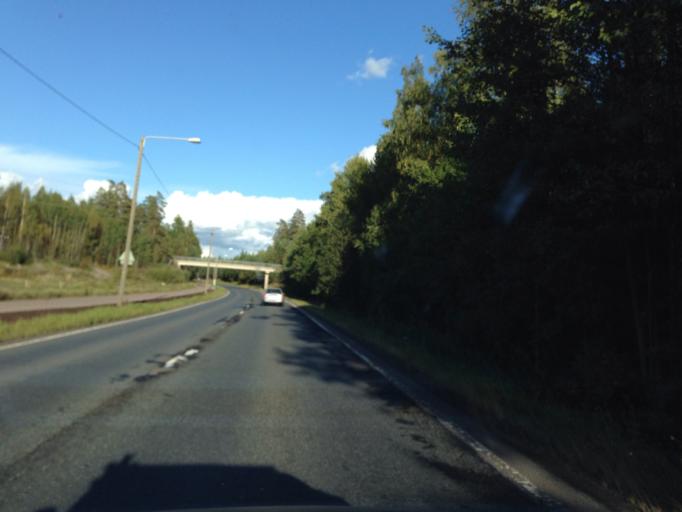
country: FI
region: Uusimaa
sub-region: Helsinki
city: Vantaa
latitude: 60.3442
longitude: 25.0315
